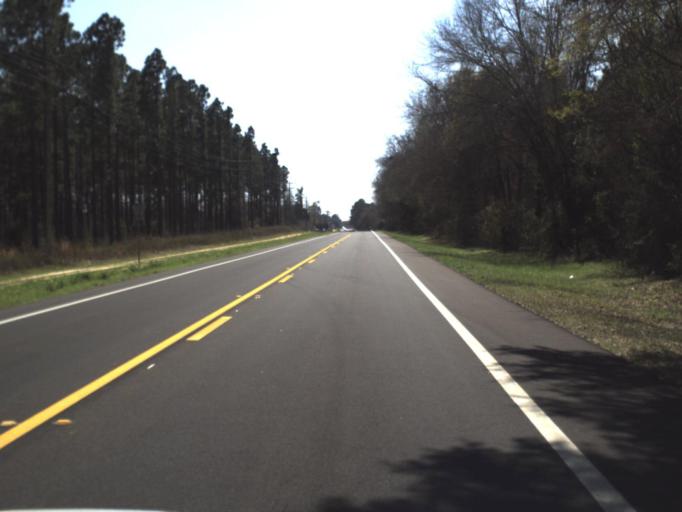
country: US
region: Florida
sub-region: Jackson County
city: Sneads
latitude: 30.7298
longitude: -85.0201
